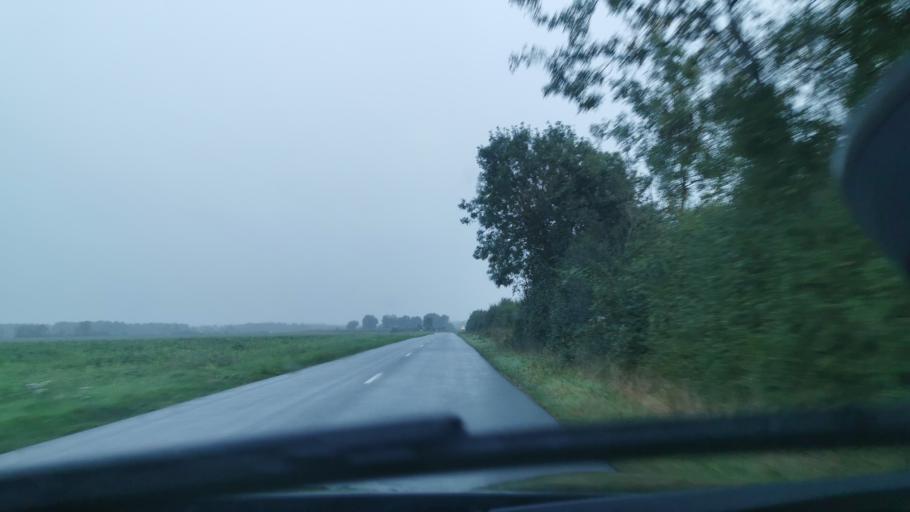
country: FR
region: Rhone-Alpes
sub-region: Departement de l'Ain
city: Amberieux-en-Dombes
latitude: 45.9624
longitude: 4.8948
